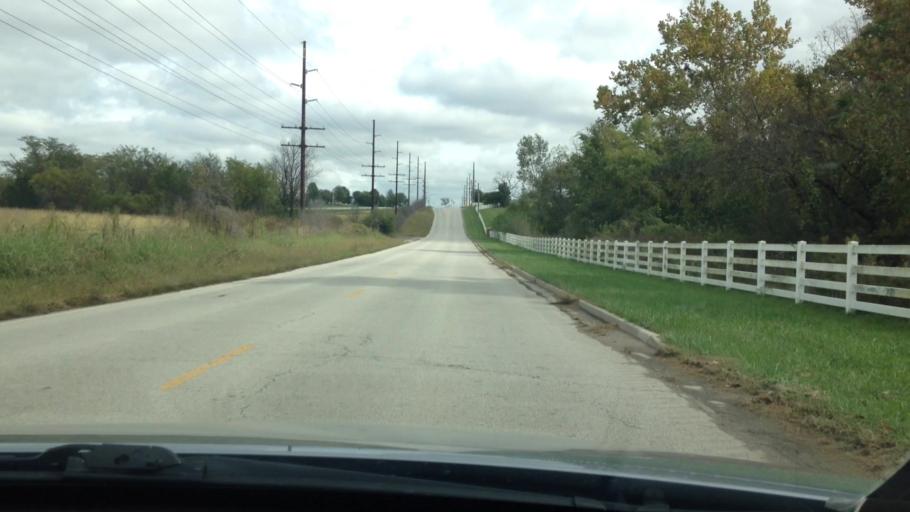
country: US
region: Missouri
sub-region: Platte County
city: Platte City
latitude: 39.3392
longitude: -94.7846
